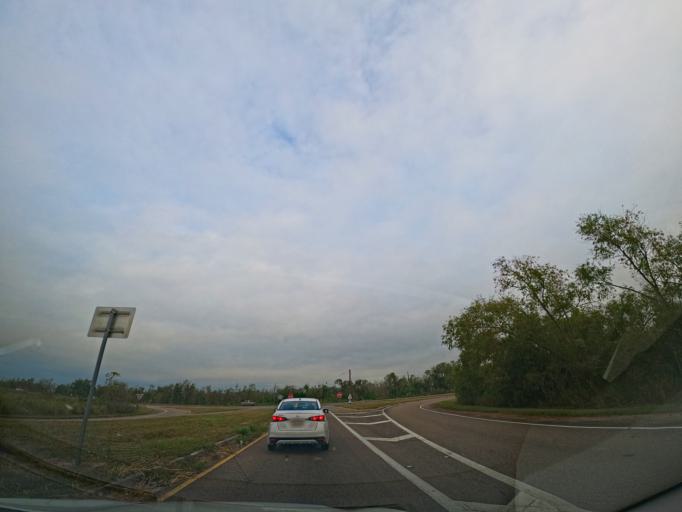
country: US
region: Louisiana
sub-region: Lafourche Parish
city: Raceland
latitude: 29.6909
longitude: -90.6363
